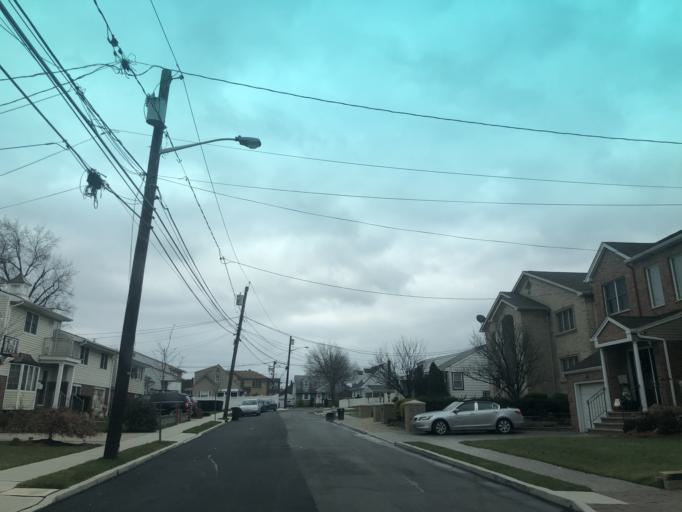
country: US
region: New Jersey
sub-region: Hudson County
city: Secaucus
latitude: 40.7993
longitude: -74.0537
